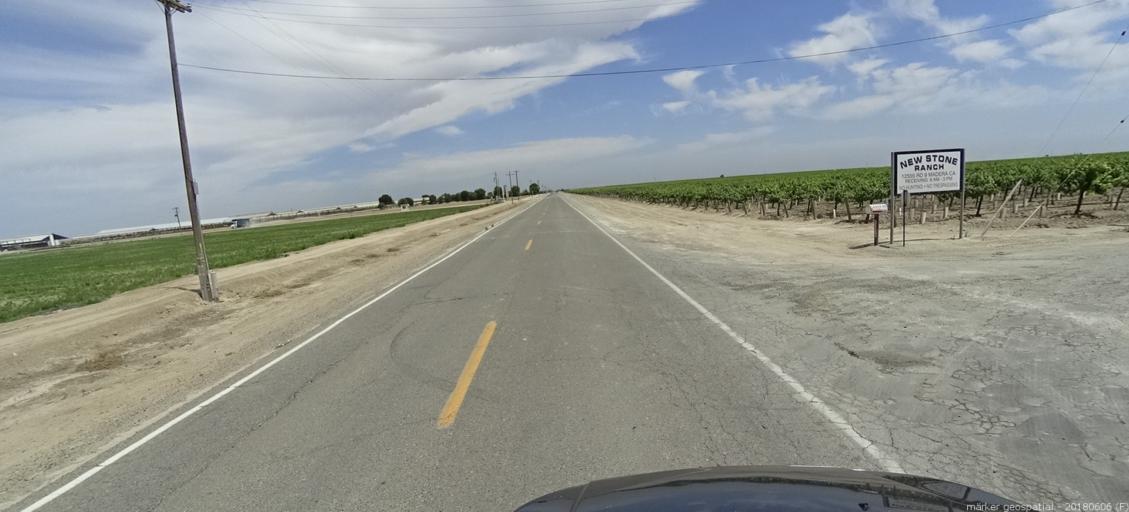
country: US
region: California
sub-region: Fresno County
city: Firebaugh
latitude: 36.9305
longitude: -120.3823
